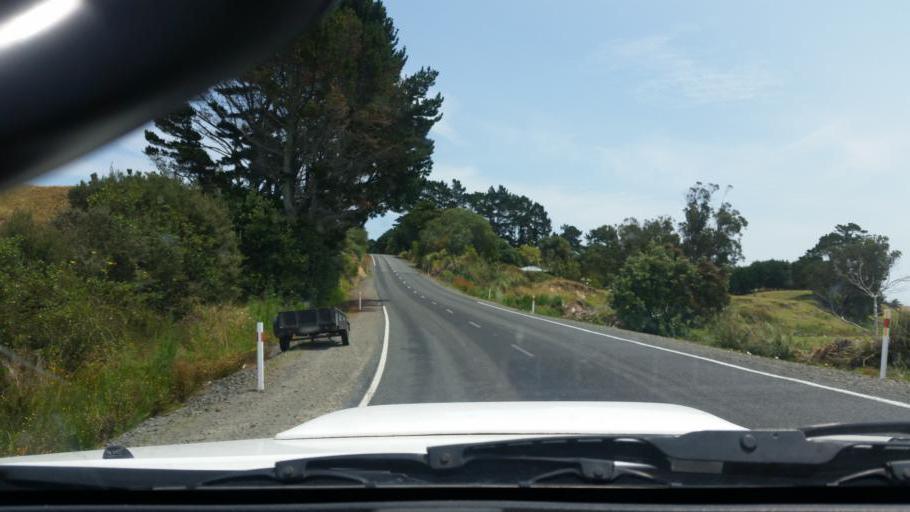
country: NZ
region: Northland
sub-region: Kaipara District
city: Dargaville
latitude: -36.1752
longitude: 174.0272
